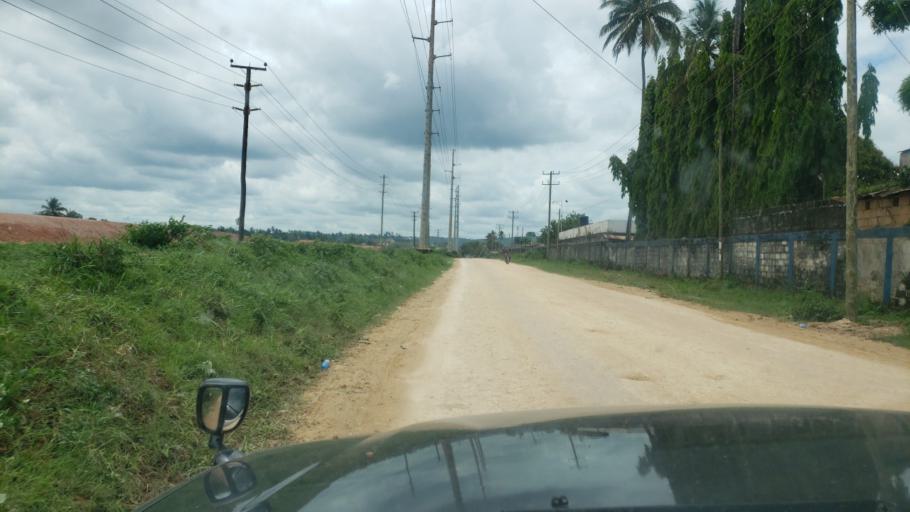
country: TZ
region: Pwani
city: Kisarawe
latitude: -6.8838
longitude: 39.1493
